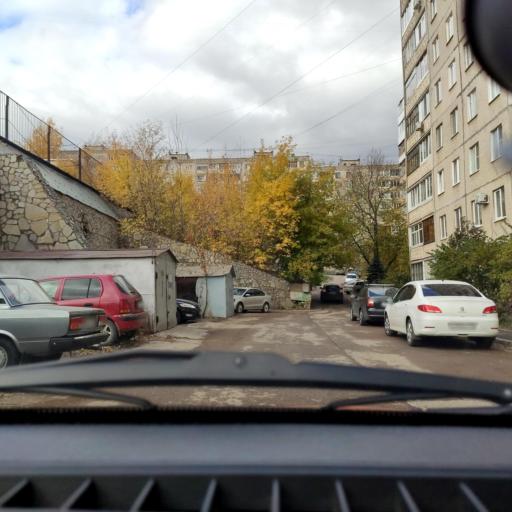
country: RU
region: Bashkortostan
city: Ufa
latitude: 54.7852
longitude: 56.0469
